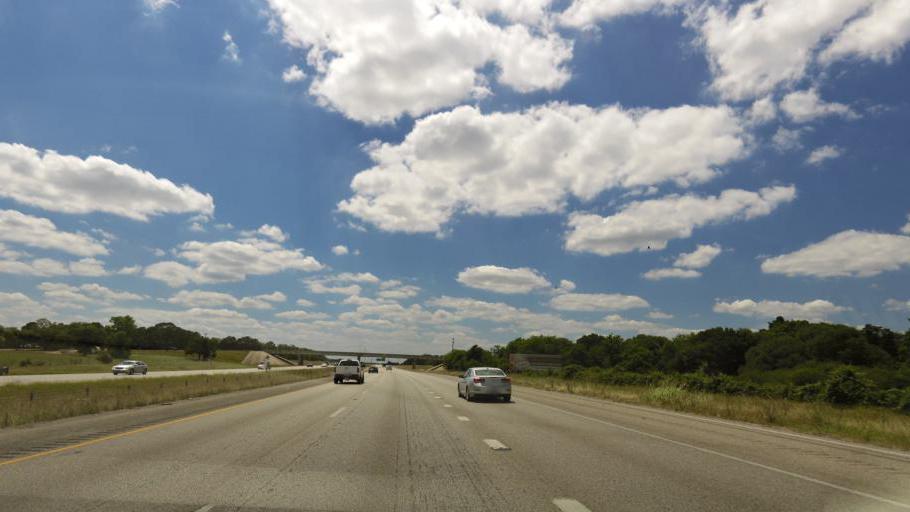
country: US
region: Texas
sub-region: Colorado County
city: Columbus
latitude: 29.6938
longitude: -96.5595
